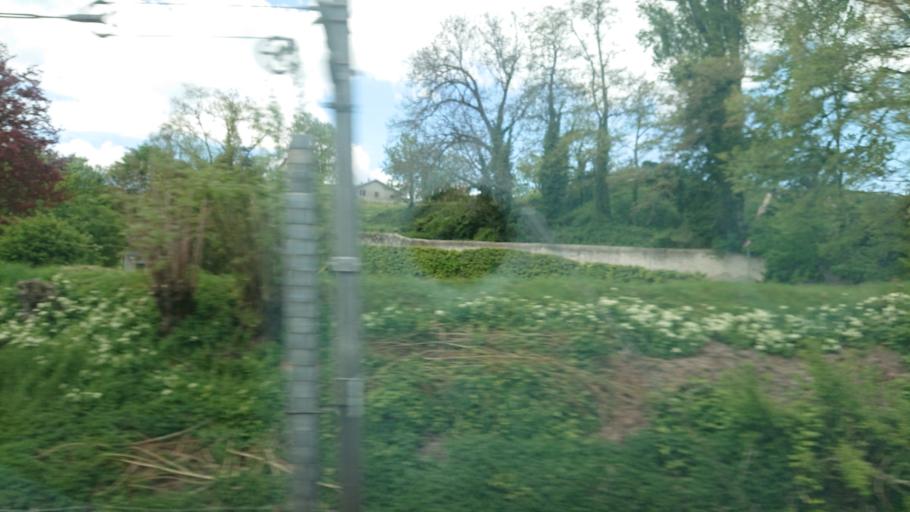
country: CH
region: Vaud
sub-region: Nyon District
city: Founex
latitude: 46.3551
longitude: 6.2084
